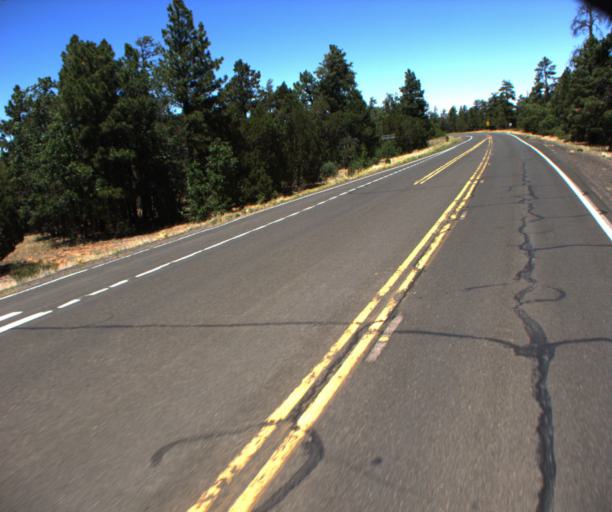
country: US
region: Arizona
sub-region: Gila County
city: Star Valley
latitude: 34.6500
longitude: -111.1086
